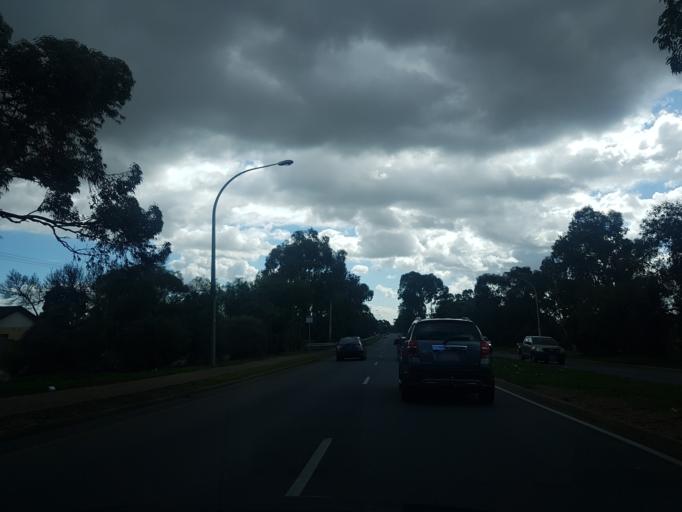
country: AU
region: South Australia
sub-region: Salisbury
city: Ingle Farm
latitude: -34.8339
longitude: 138.6455
